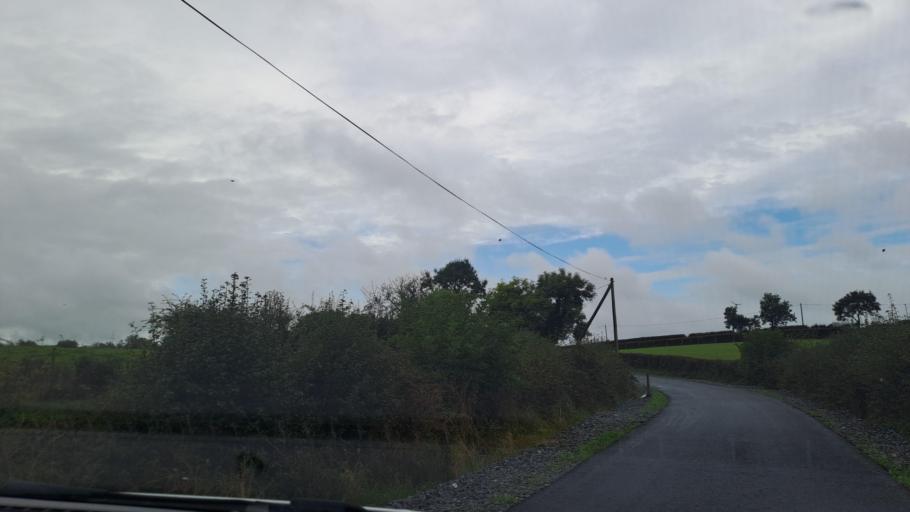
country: IE
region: Ulster
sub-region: An Cabhan
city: Kingscourt
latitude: 53.9811
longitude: -6.8347
